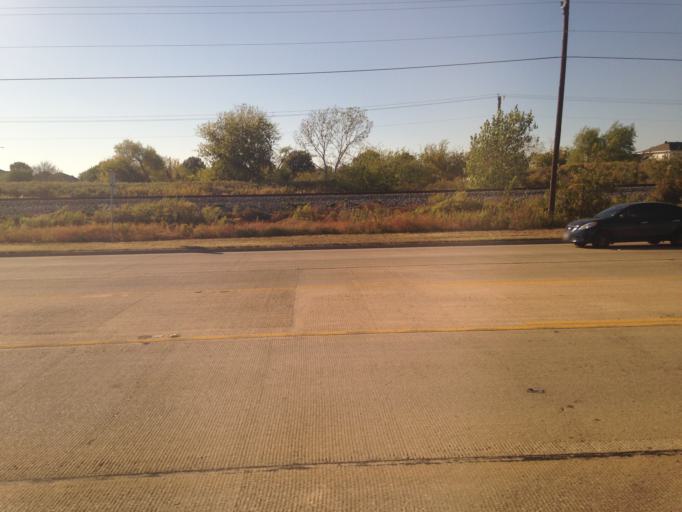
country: US
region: Texas
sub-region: Tarrant County
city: Watauga
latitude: 32.8795
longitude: -97.2609
